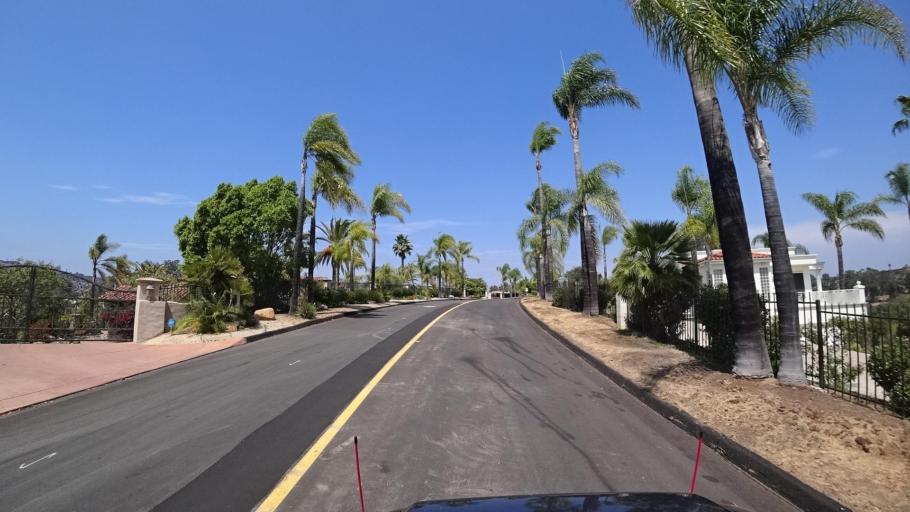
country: US
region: California
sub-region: San Diego County
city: Bonsall
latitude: 33.3056
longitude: -117.2176
